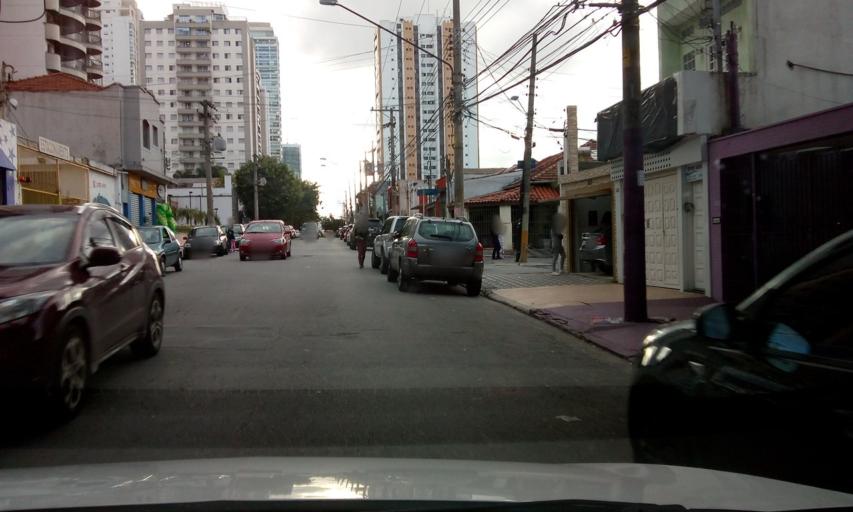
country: BR
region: Sao Paulo
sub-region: Sao Paulo
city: Sao Paulo
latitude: -23.5458
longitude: -46.5672
